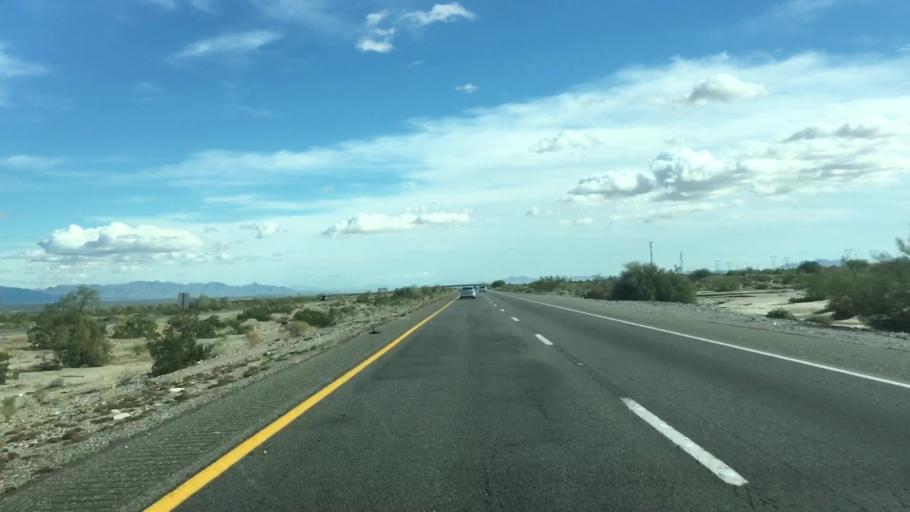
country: US
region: California
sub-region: Imperial County
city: Niland
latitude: 33.6869
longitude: -115.2588
